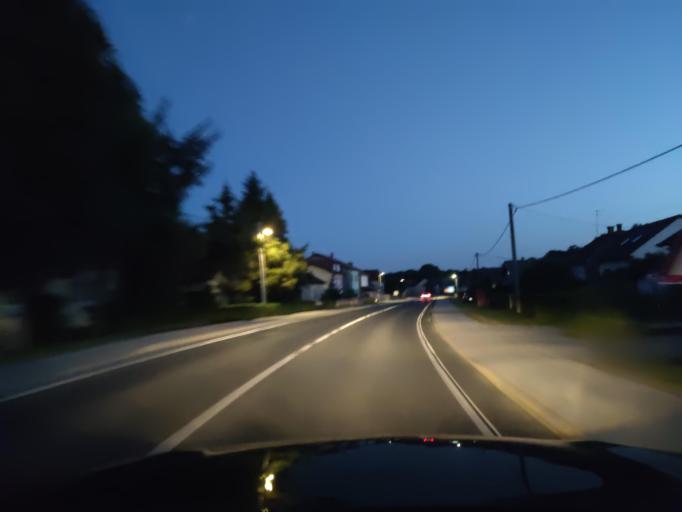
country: HR
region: Medimurska
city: Mackovec
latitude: 46.4307
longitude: 16.4311
